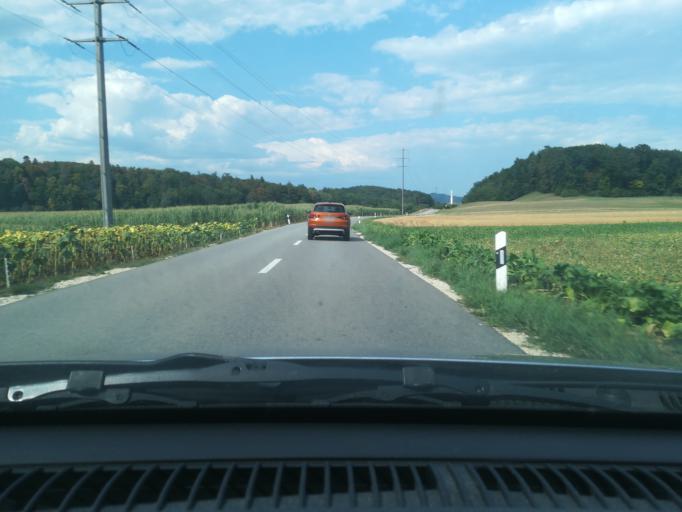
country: CH
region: Schaffhausen
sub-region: Bezirk Reiat
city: Stetten
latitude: 47.7381
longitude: 8.6771
